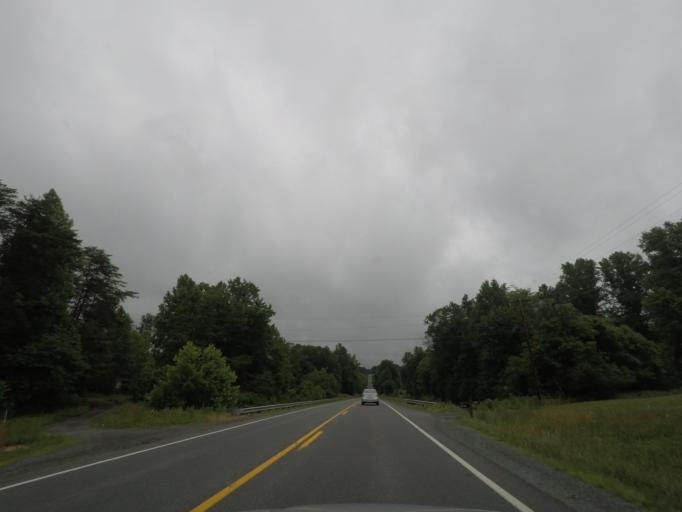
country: US
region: Virginia
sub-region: Fluvanna County
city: Palmyra
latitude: 37.8371
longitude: -78.2735
